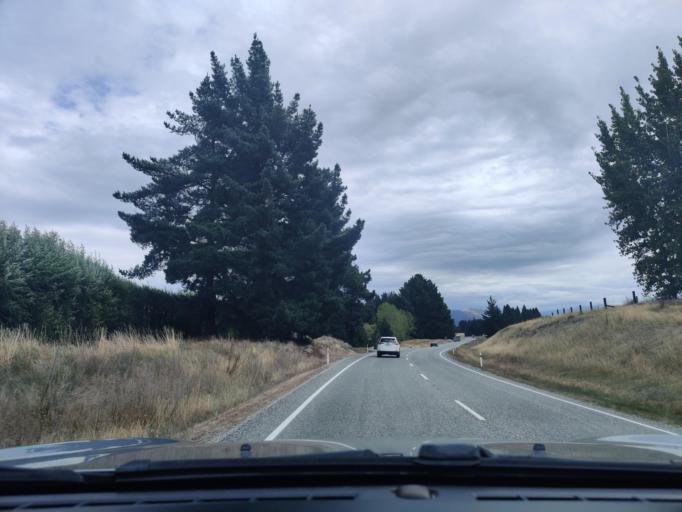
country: NZ
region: Otago
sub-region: Queenstown-Lakes District
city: Wanaka
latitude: -44.7137
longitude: 169.2106
